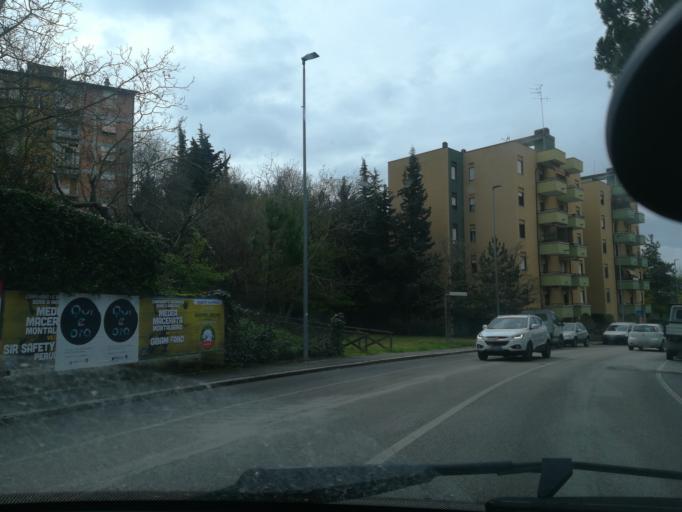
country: IT
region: The Marches
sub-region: Provincia di Macerata
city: Macerata
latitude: 43.2835
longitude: 13.4309
